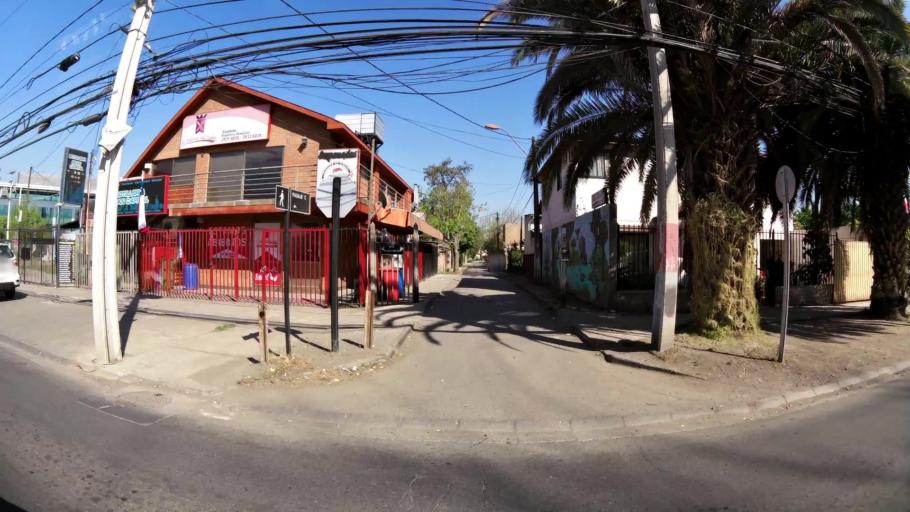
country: CL
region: Santiago Metropolitan
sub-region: Provincia de Chacabuco
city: Chicureo Abajo
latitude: -33.3607
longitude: -70.6706
